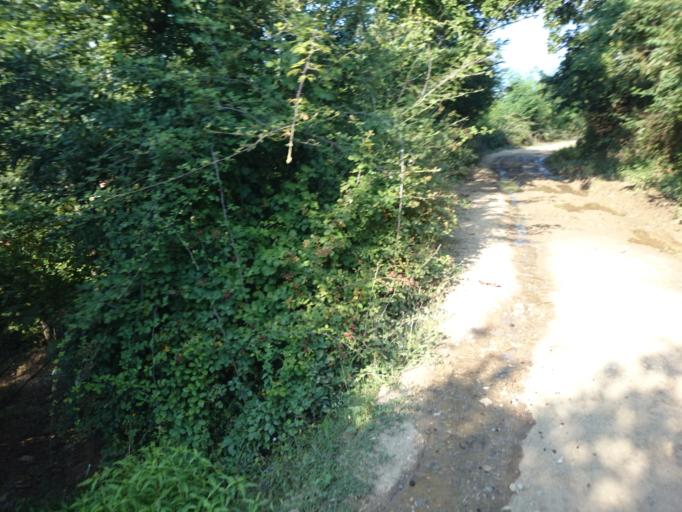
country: AL
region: Diber
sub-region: Rrethi i Dibres
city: Arras
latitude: 41.7362
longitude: 20.3244
